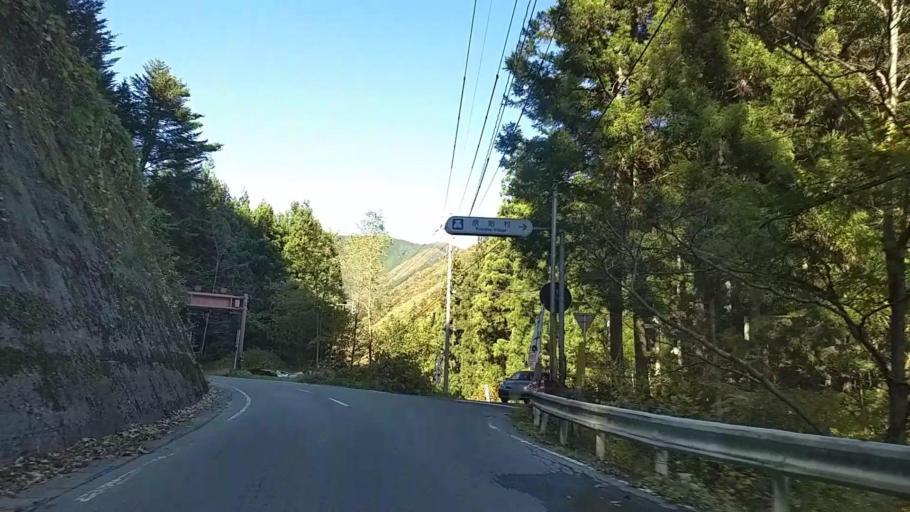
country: JP
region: Yamanashi
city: Otsuki
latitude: 35.7435
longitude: 138.9661
